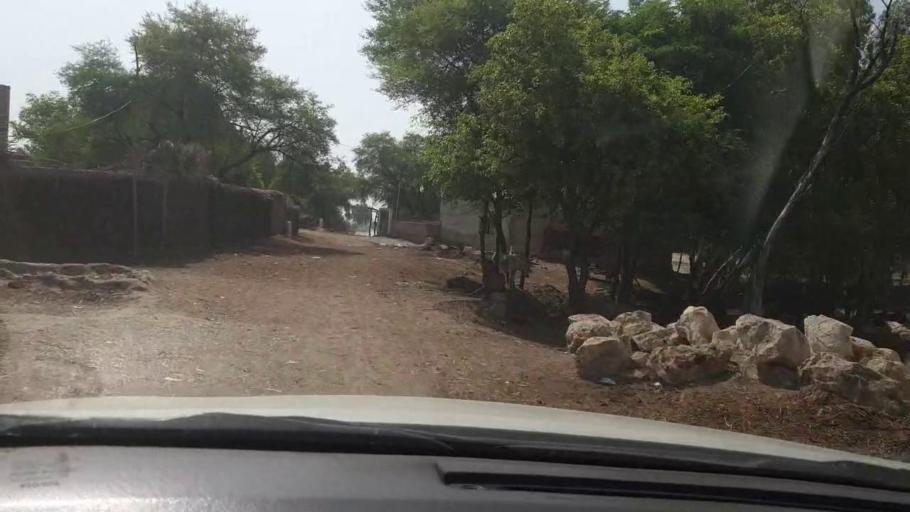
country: PK
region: Sindh
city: Rustam jo Goth
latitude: 27.9730
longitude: 68.7786
